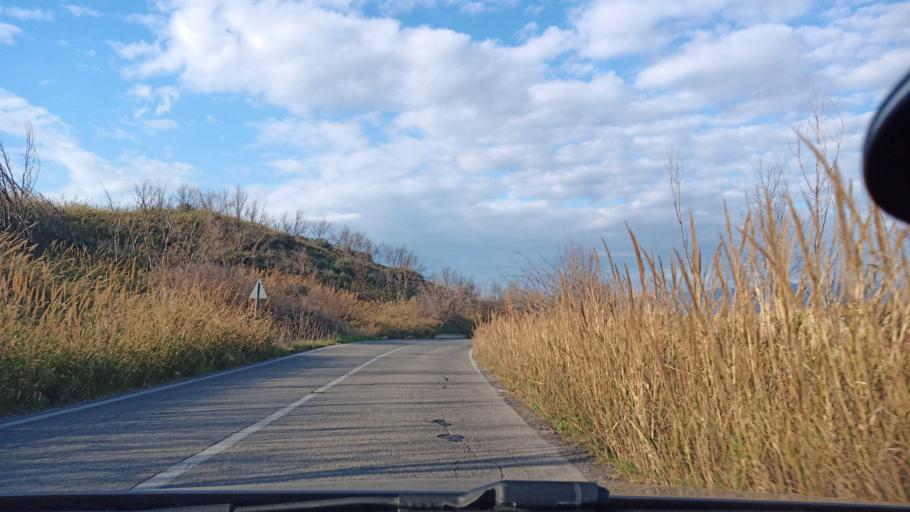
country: IT
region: Latium
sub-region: Citta metropolitana di Roma Capitale
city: Civitella San Paolo
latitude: 42.1946
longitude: 12.6047
